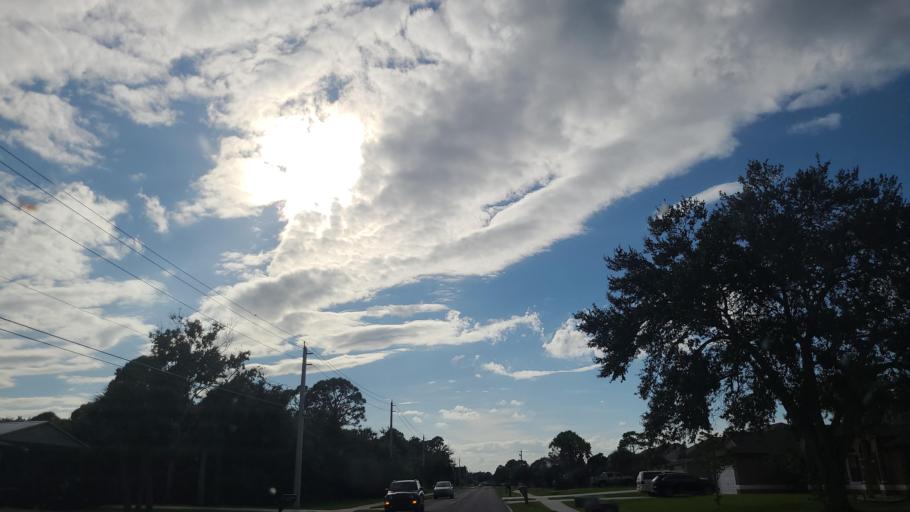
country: US
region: Florida
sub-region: Brevard County
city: June Park
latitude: 28.0109
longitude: -80.6775
